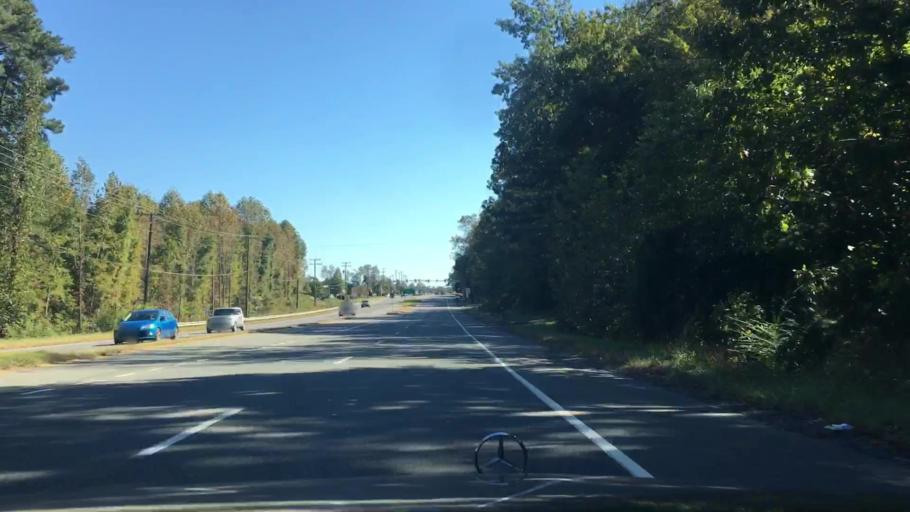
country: US
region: Virginia
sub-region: King George County
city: King George
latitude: 38.2789
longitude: -77.2153
